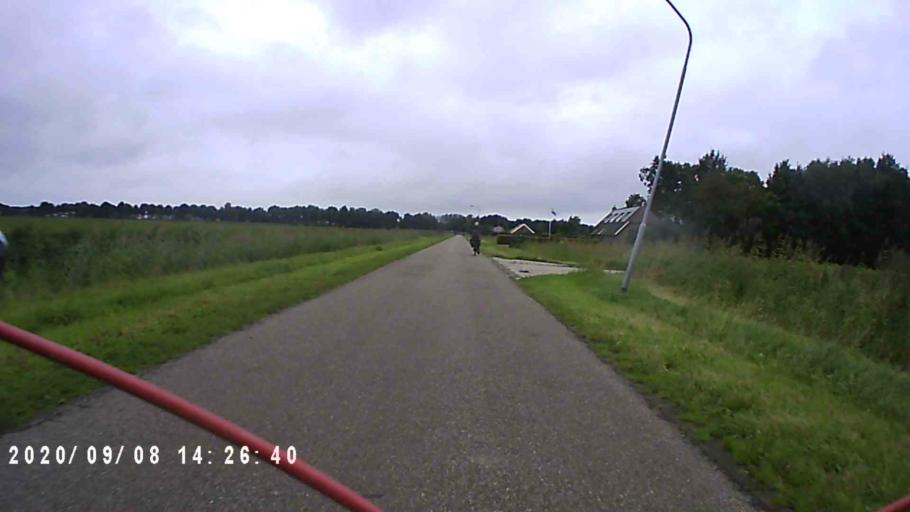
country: NL
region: Groningen
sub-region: Gemeente Slochteren
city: Slochteren
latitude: 53.2211
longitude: 6.8208
